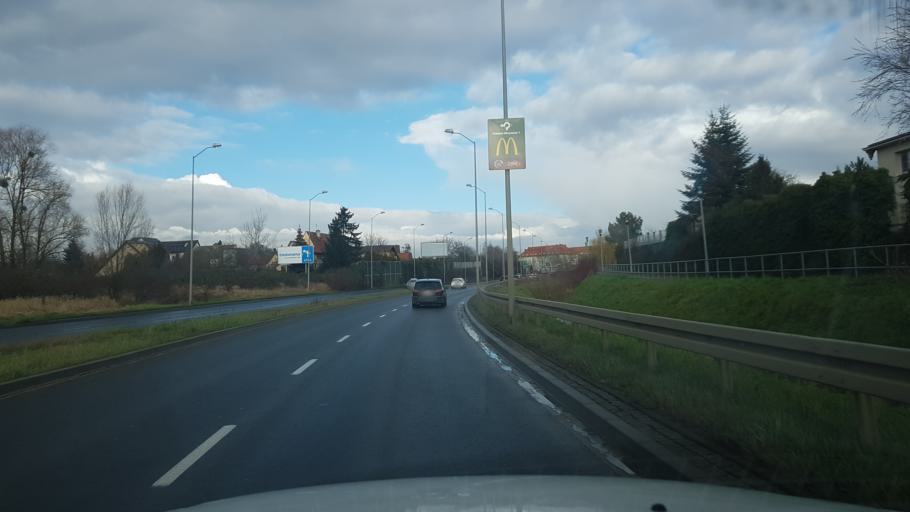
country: PL
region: West Pomeranian Voivodeship
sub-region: Powiat policki
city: Przeclaw
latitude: 53.4183
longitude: 14.4957
